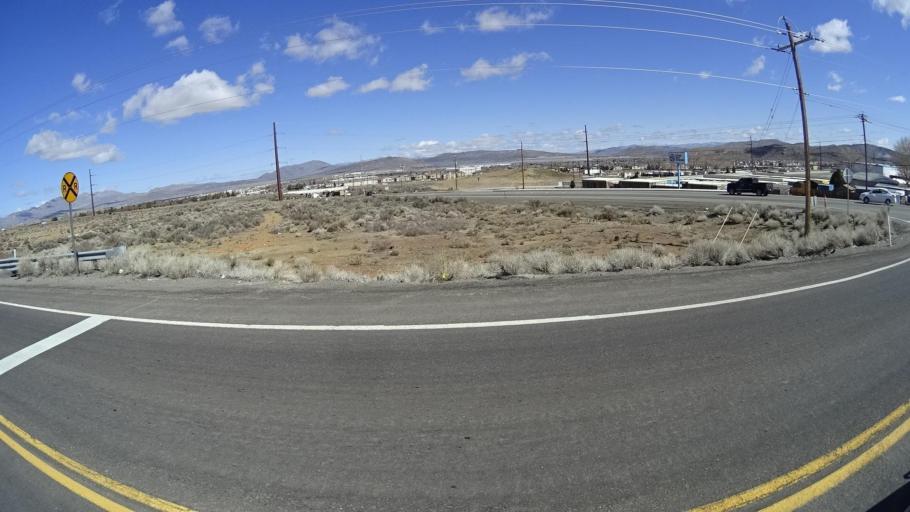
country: US
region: Nevada
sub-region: Washoe County
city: Lemmon Valley
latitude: 39.6148
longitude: -119.8818
